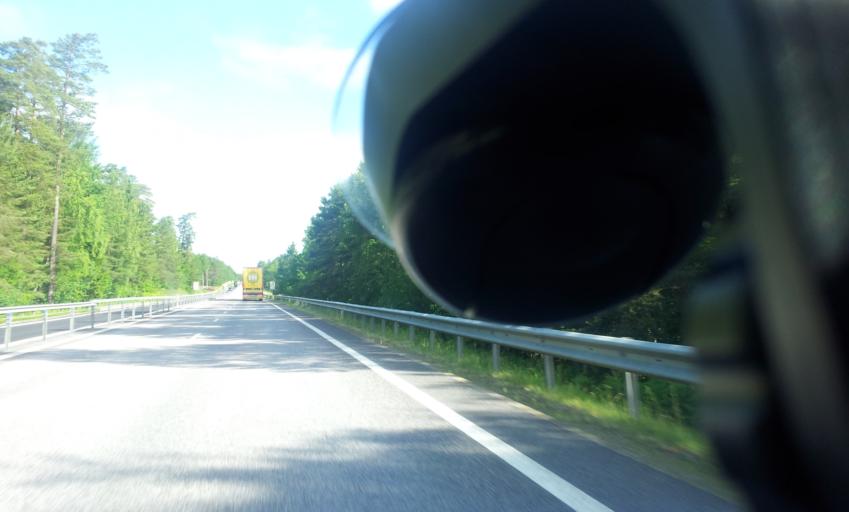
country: SE
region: Kalmar
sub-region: Kalmar Kommun
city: Lindsdal
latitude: 56.8204
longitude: 16.3693
